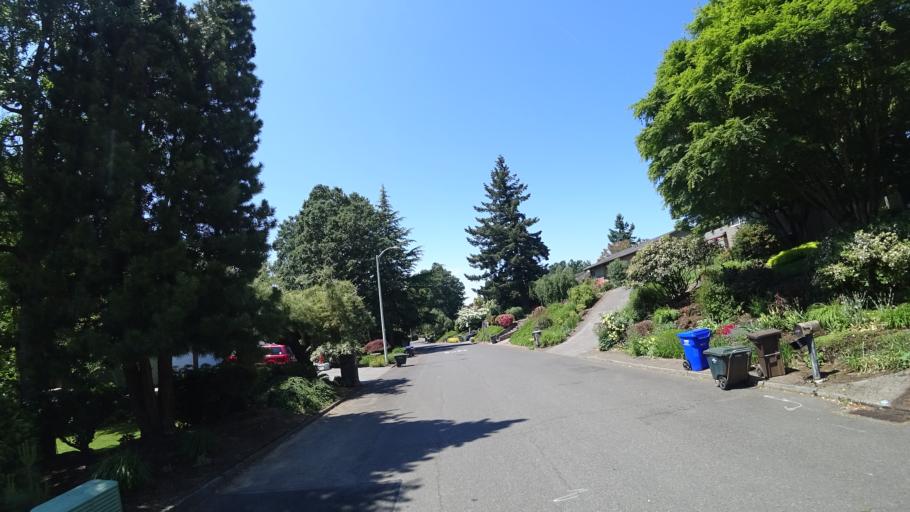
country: US
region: Oregon
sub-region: Multnomah County
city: Fairview
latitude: 45.5527
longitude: -122.4540
